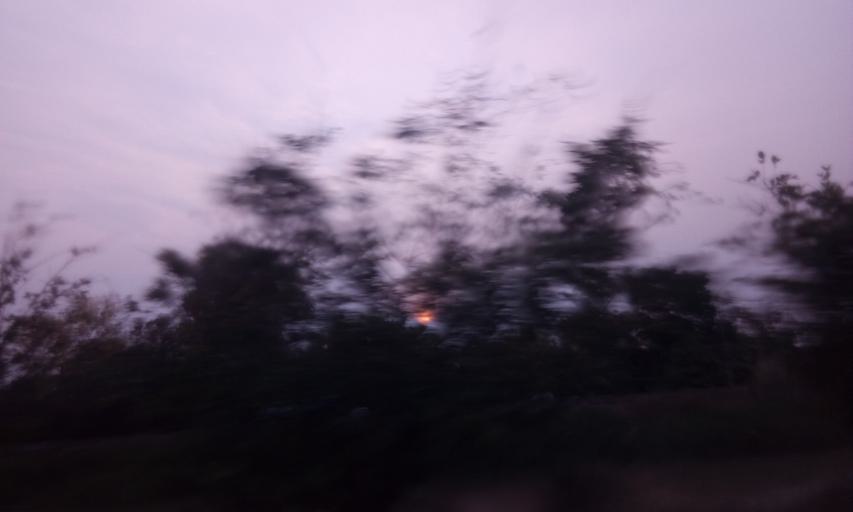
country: TH
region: Pathum Thani
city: Ban Lam Luk Ka
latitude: 14.0094
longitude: 100.8945
